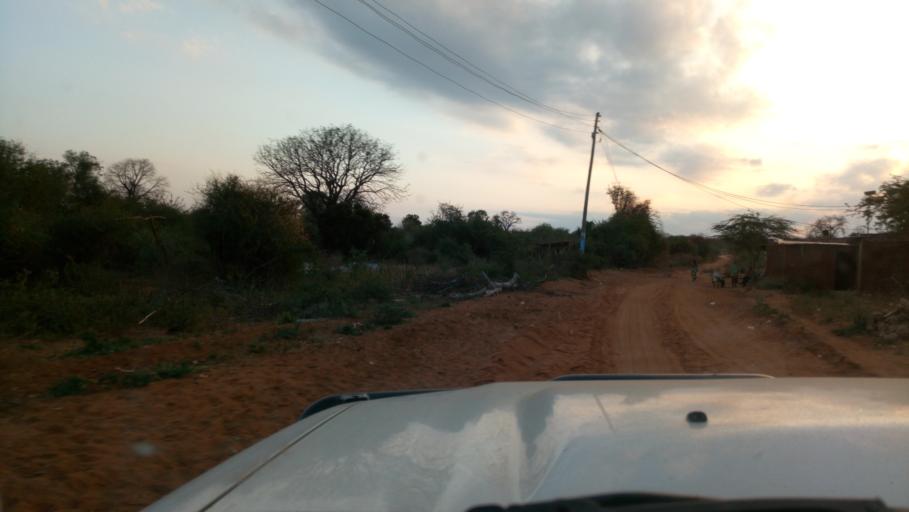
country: KE
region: Kitui
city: Kitui
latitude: -1.7168
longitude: 38.2507
